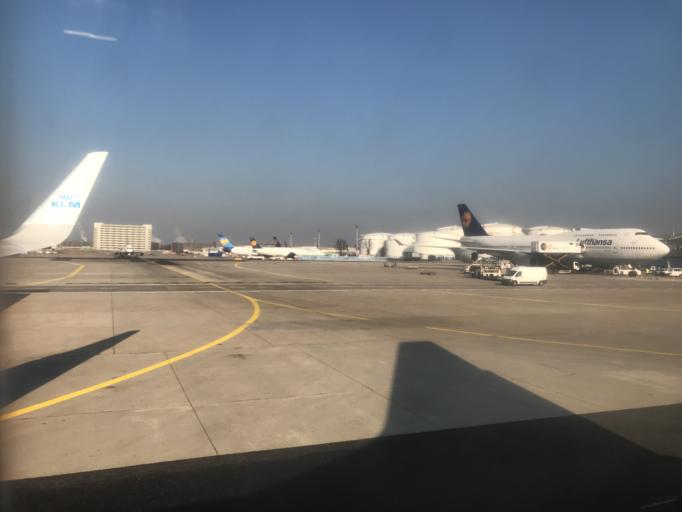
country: DE
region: Hesse
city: Kelsterbach
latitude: 50.0383
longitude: 8.5506
